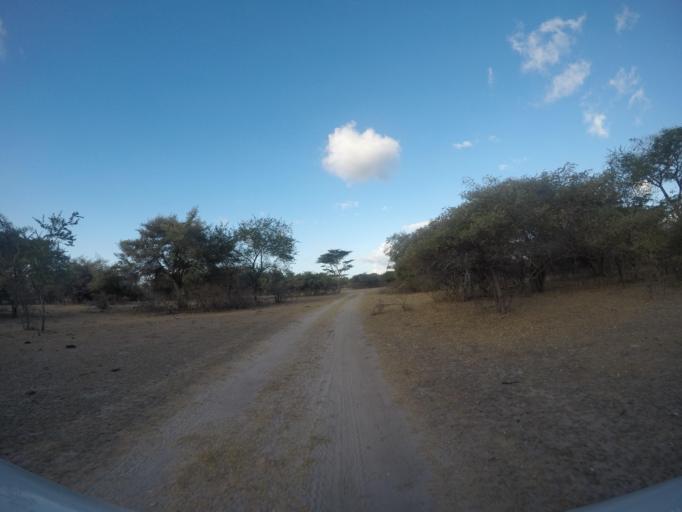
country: TL
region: Lautem
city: Lospalos
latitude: -8.3254
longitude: 126.9850
